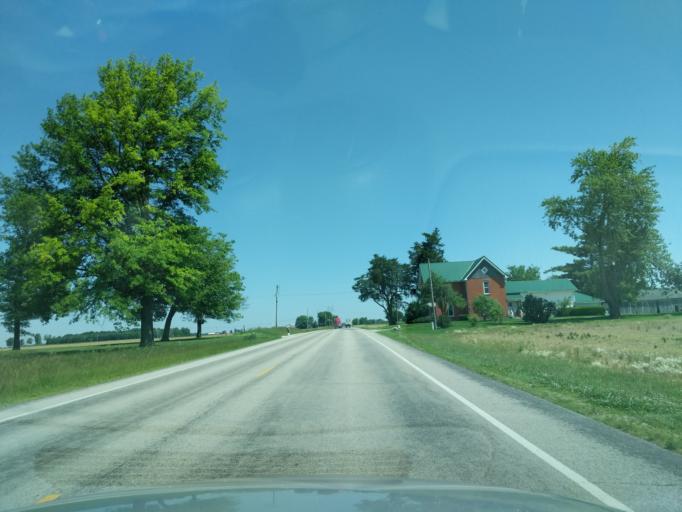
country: US
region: Indiana
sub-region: Huntington County
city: Huntington
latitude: 40.9265
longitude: -85.4709
